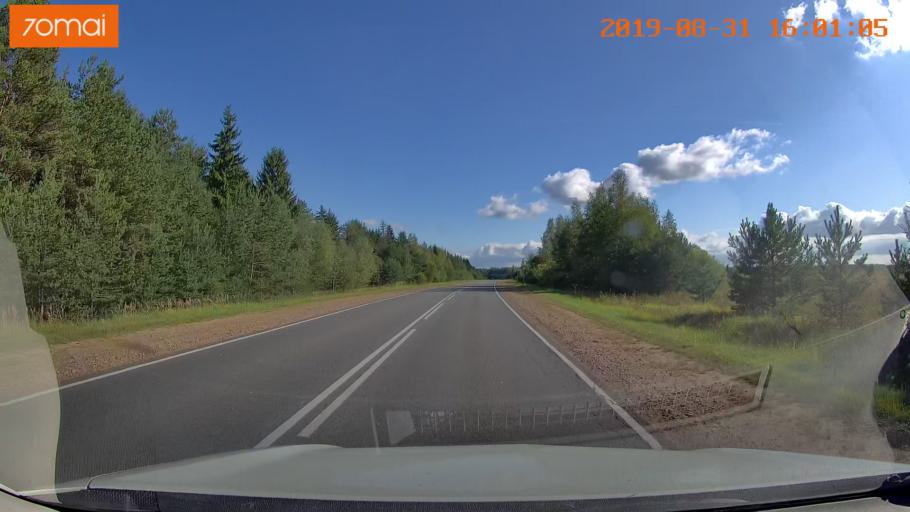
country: RU
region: Kaluga
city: Yukhnov
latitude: 54.6954
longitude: 35.2880
